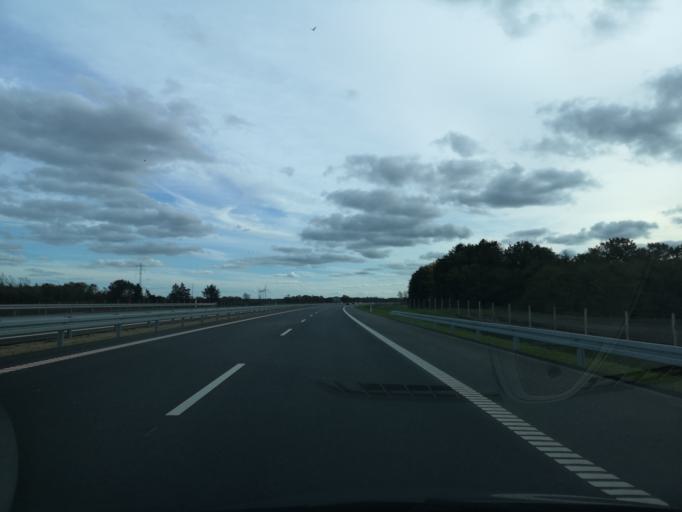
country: DK
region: Central Jutland
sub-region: Herning Kommune
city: Avlum
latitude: 56.3567
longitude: 8.7340
